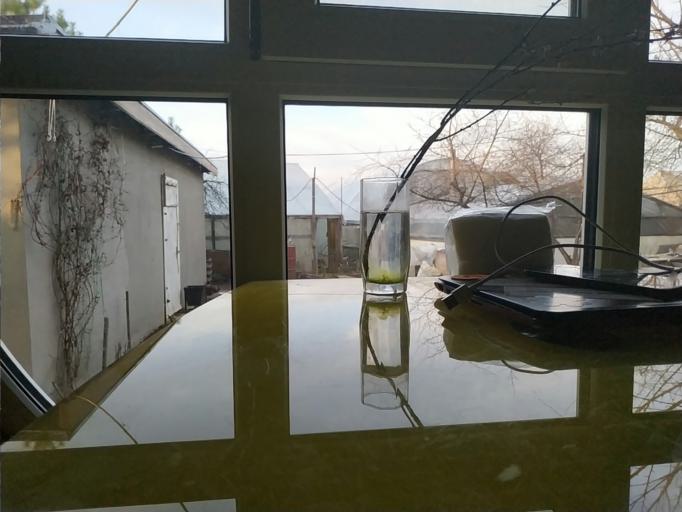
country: RU
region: Republic of Karelia
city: Suoyarvi
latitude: 62.2992
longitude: 32.0729
